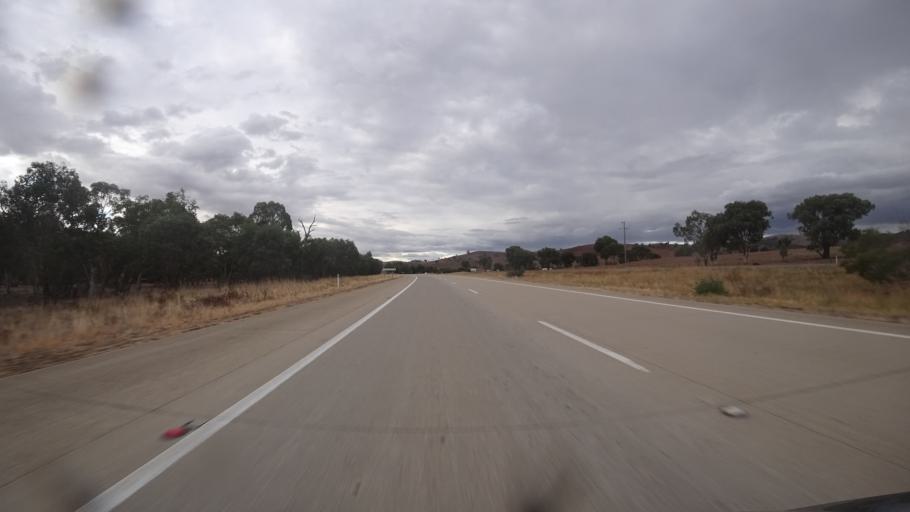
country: AU
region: New South Wales
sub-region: Yass Valley
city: Yass
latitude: -34.8066
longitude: 148.6917
